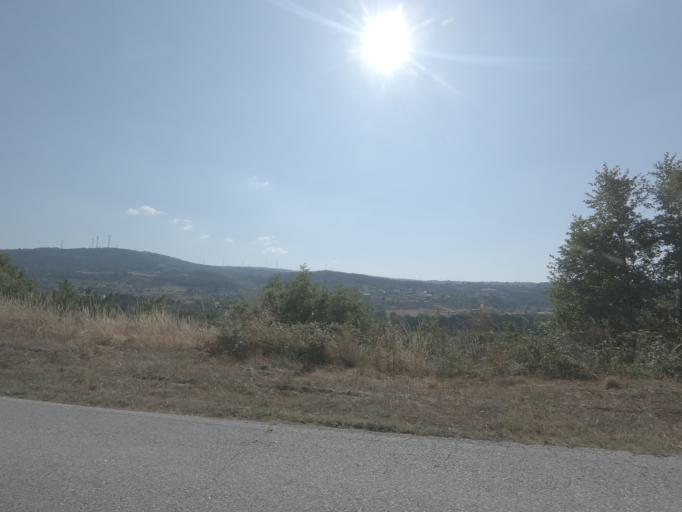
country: PT
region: Viseu
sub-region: Moimenta da Beira
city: Moimenta da Beira
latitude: 40.9777
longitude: -7.5783
